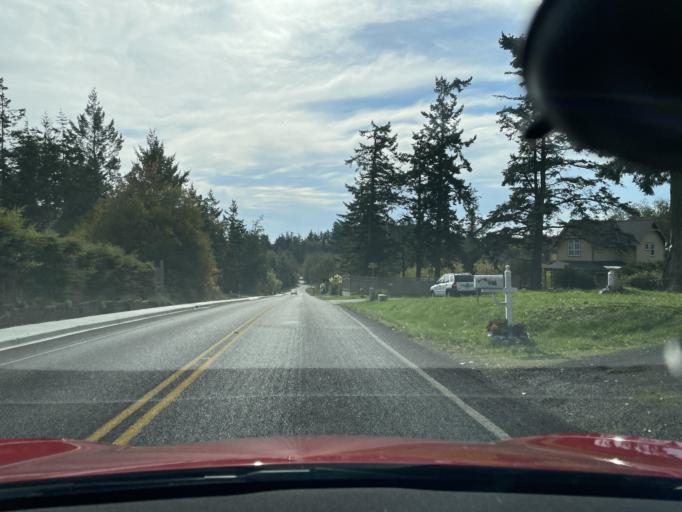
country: US
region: Washington
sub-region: San Juan County
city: Friday Harbor
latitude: 48.5248
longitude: -123.0177
